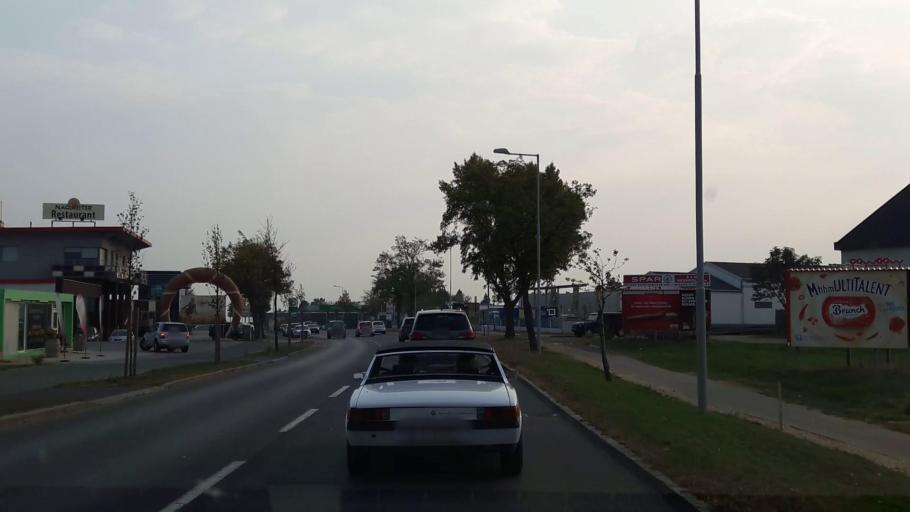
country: AT
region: Burgenland
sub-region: Politischer Bezirk Neusiedl am See
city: Neusiedl am See
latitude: 47.9602
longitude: 16.8359
